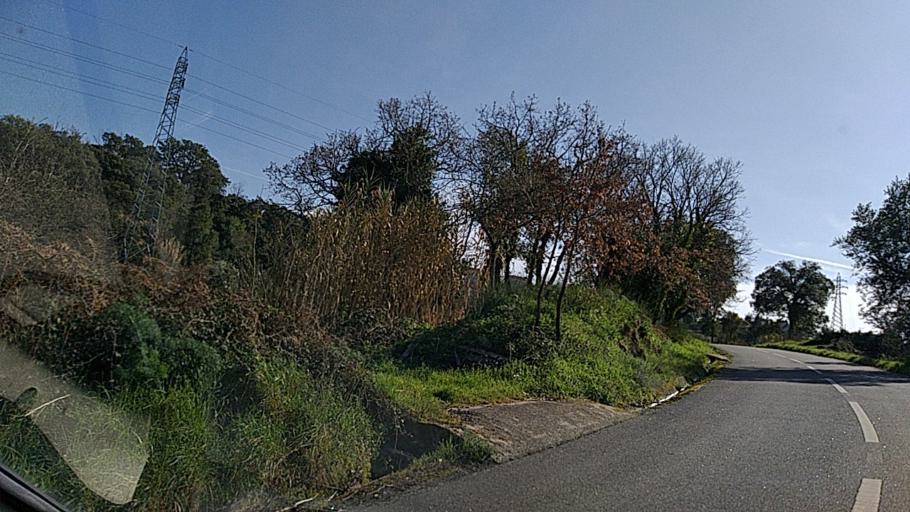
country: PT
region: Guarda
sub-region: Celorico da Beira
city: Celorico da Beira
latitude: 40.6372
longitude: -7.3973
